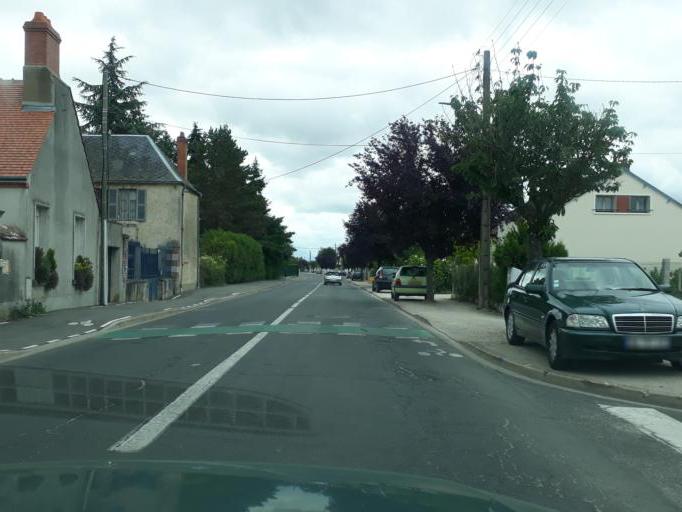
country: FR
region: Centre
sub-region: Departement du Loiret
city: Saint-Jean-le-Blanc
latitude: 47.8773
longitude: 1.9329
